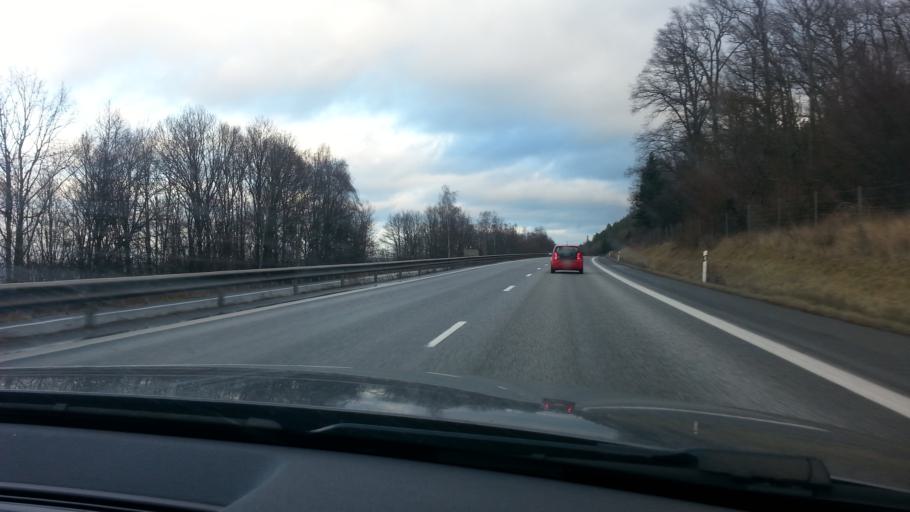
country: SE
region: Joenkoeping
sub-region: Jonkopings Kommun
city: Kaxholmen
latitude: 57.8797
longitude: 14.2782
